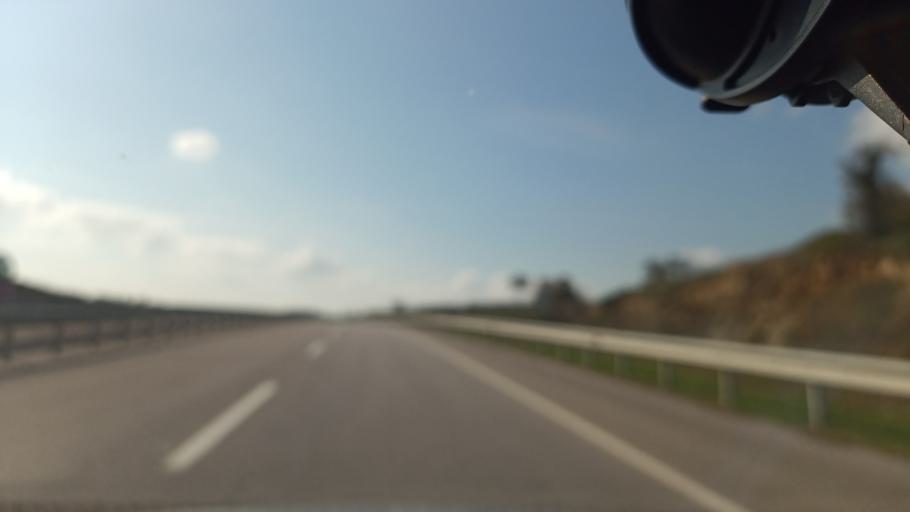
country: TR
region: Sakarya
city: Kaynarca
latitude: 41.0566
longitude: 30.3482
